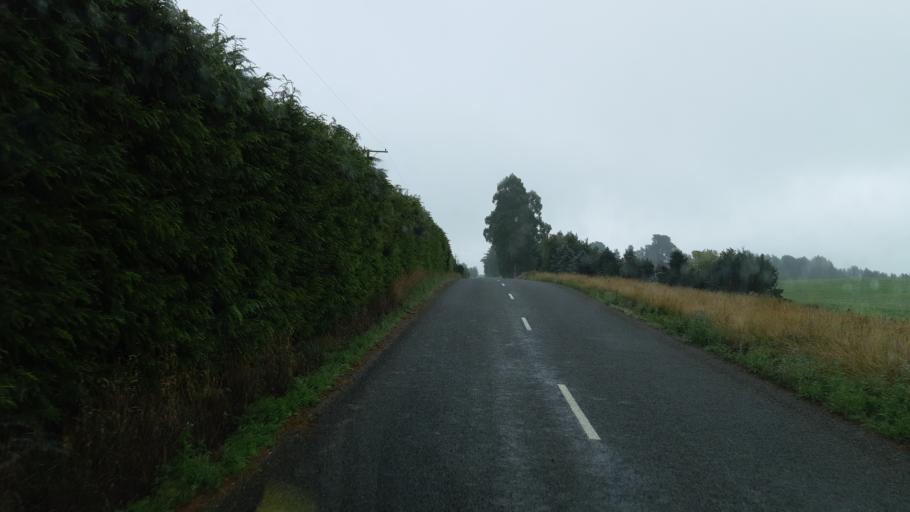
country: NZ
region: Otago
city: Oamaru
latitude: -44.9379
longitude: 170.7225
